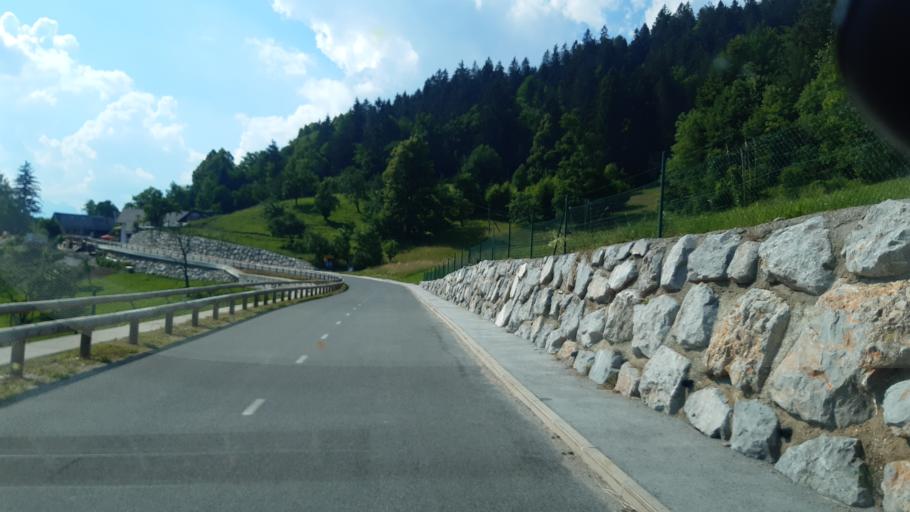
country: SI
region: Trzic
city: Bistrica pri Trzicu
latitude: 46.3630
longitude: 14.2395
